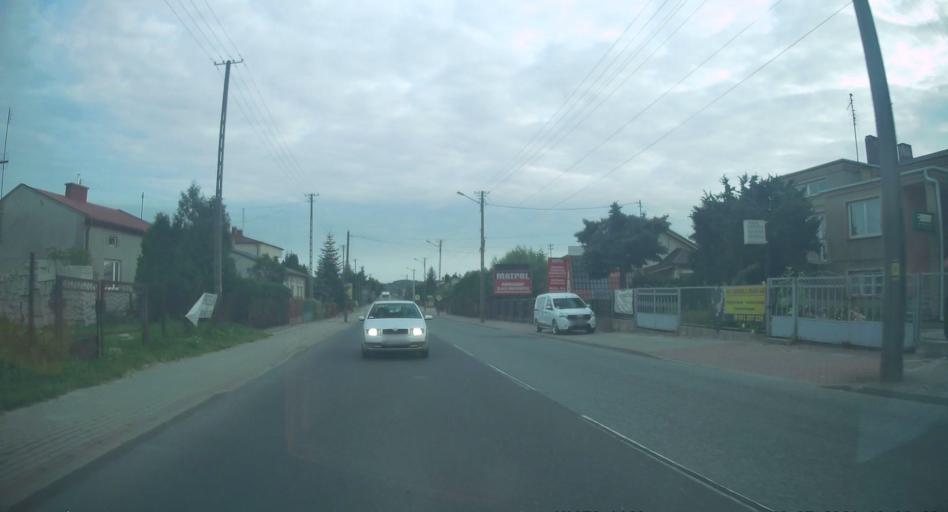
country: PL
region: Lodz Voivodeship
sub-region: Powiat radomszczanski
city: Kamiensk
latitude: 51.1999
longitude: 19.4998
